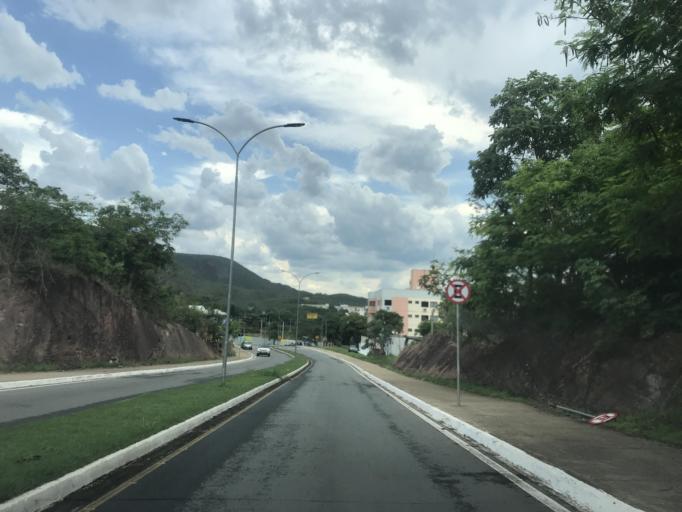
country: BR
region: Goias
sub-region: Caldas Novas
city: Caldas Novas
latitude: -17.7685
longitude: -48.7550
